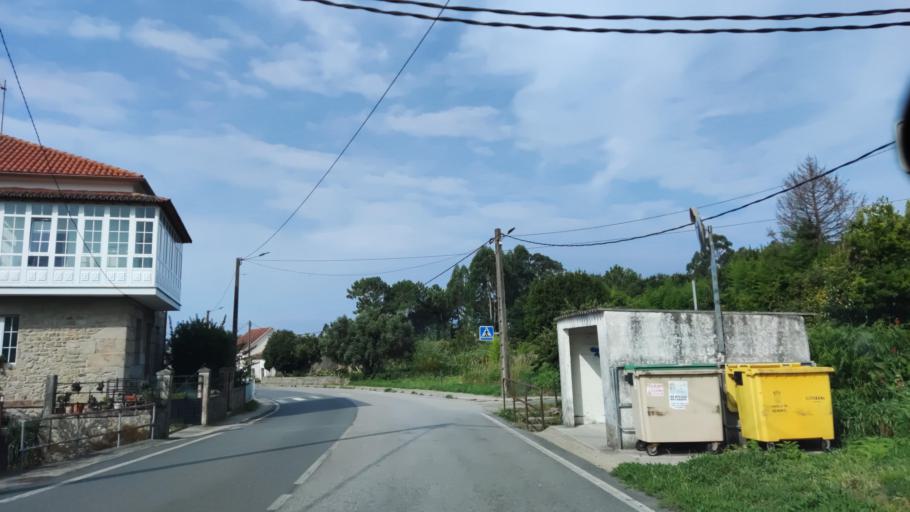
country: ES
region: Galicia
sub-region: Provincia da Coruna
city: Rianxo
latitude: 42.6478
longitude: -8.7964
